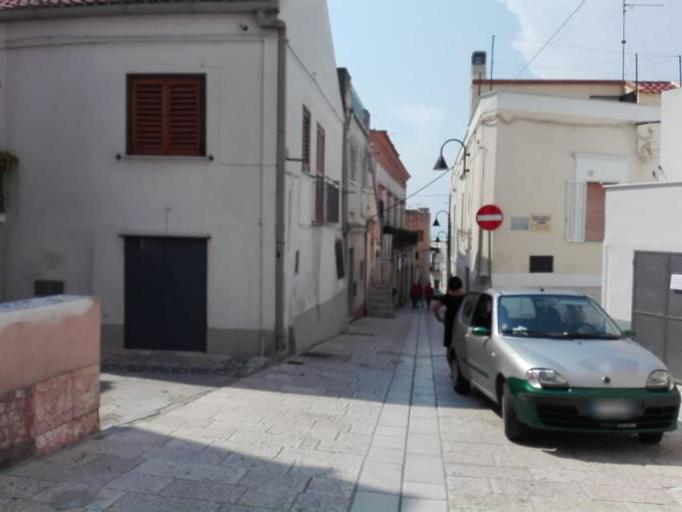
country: IT
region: Basilicate
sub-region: Provincia di Matera
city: Miglionico
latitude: 40.5696
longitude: 16.4995
